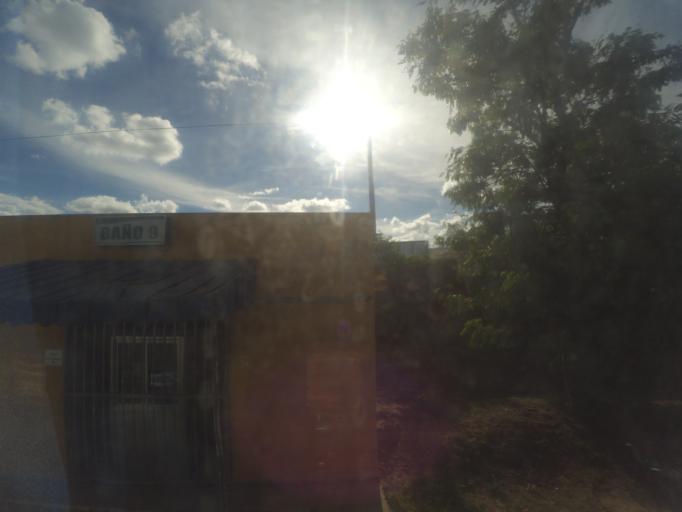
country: BO
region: Santa Cruz
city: Santa Cruz de la Sierra
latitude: -17.7880
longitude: -63.1617
